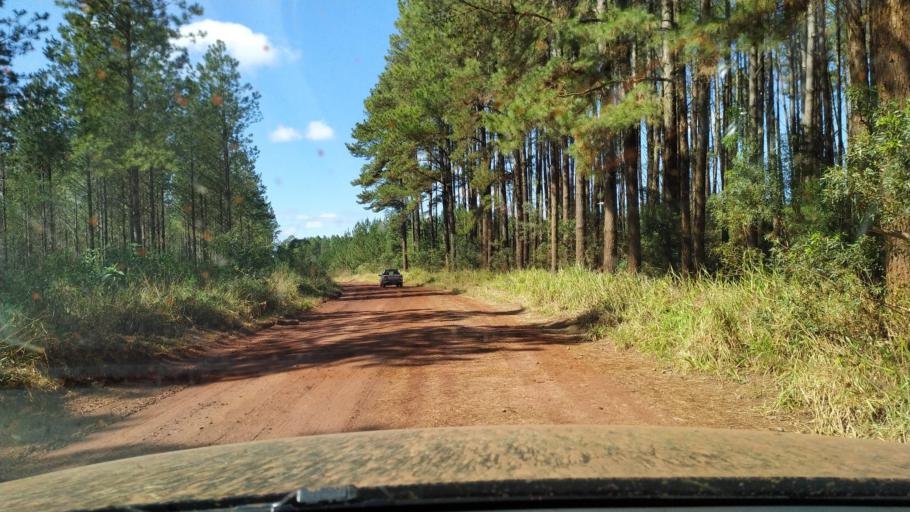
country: AR
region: Corrientes
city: Santo Tome
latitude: -28.4016
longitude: -56.0158
